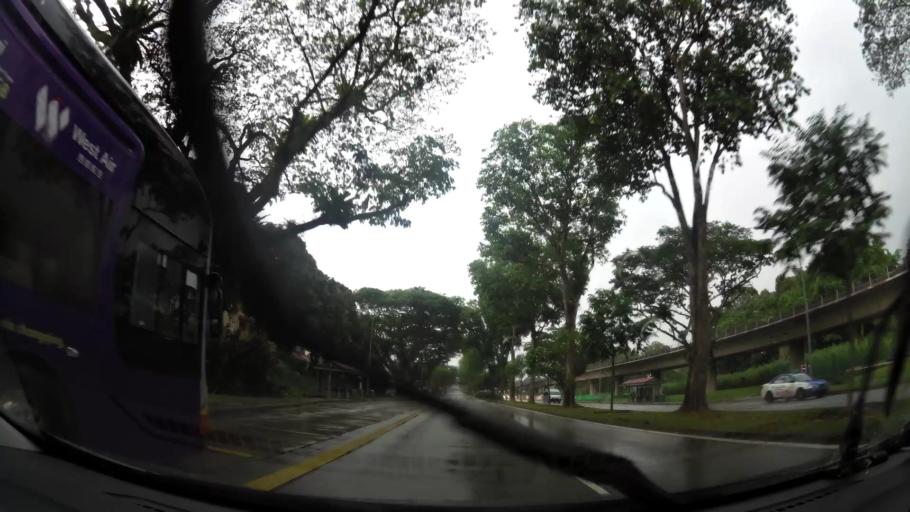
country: MY
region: Johor
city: Kampung Pasir Gudang Baru
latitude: 1.3910
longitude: 103.8389
